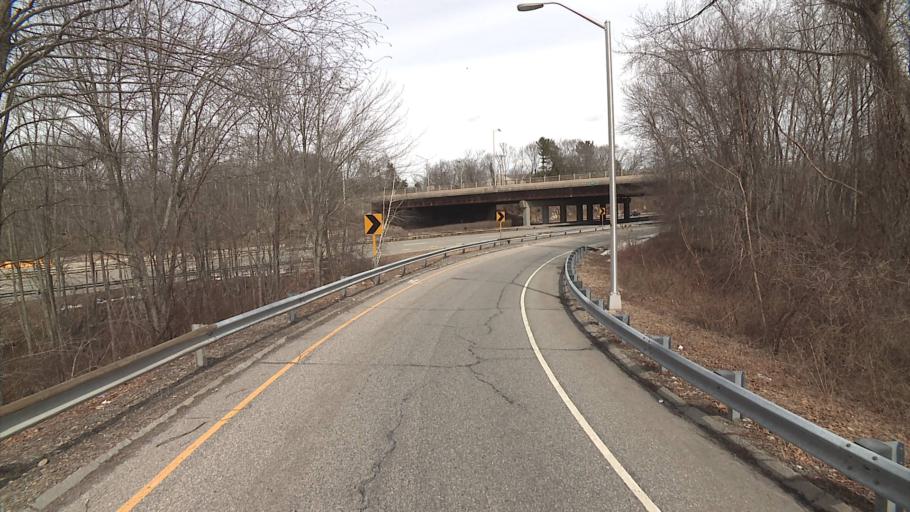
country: US
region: Connecticut
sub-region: New London County
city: Long Hill
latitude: 41.3593
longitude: -72.0647
